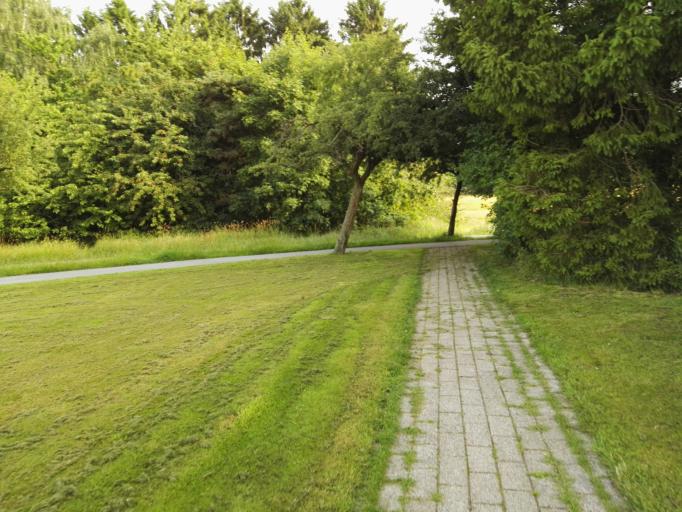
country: DK
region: Capital Region
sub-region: Ballerup Kommune
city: Ballerup
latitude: 55.7421
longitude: 12.3622
